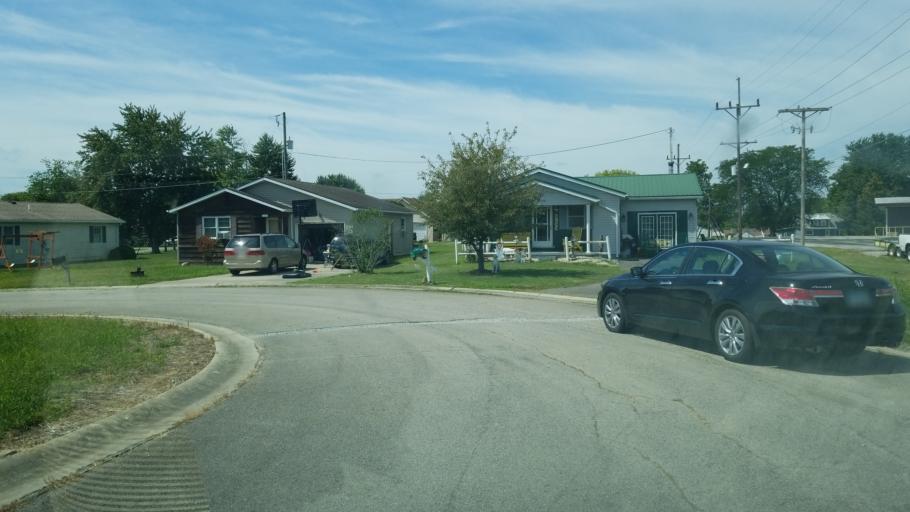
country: US
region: Ohio
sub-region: Hardin County
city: Kenton
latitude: 40.6432
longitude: -83.5950
